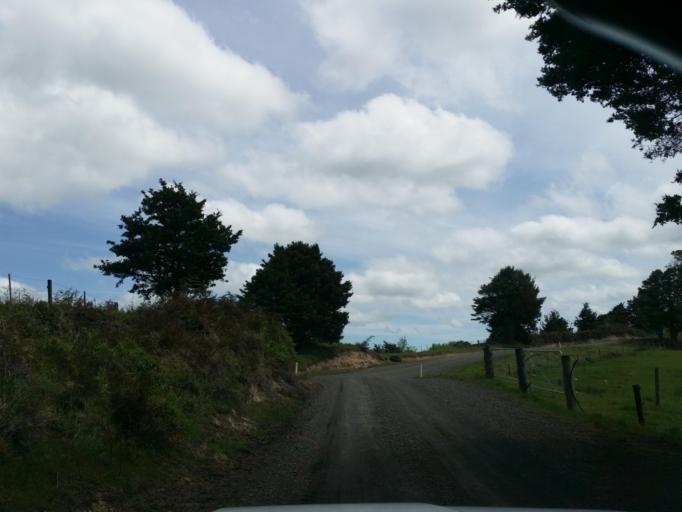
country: NZ
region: Northland
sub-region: Kaipara District
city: Dargaville
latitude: -35.9099
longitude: 174.0470
